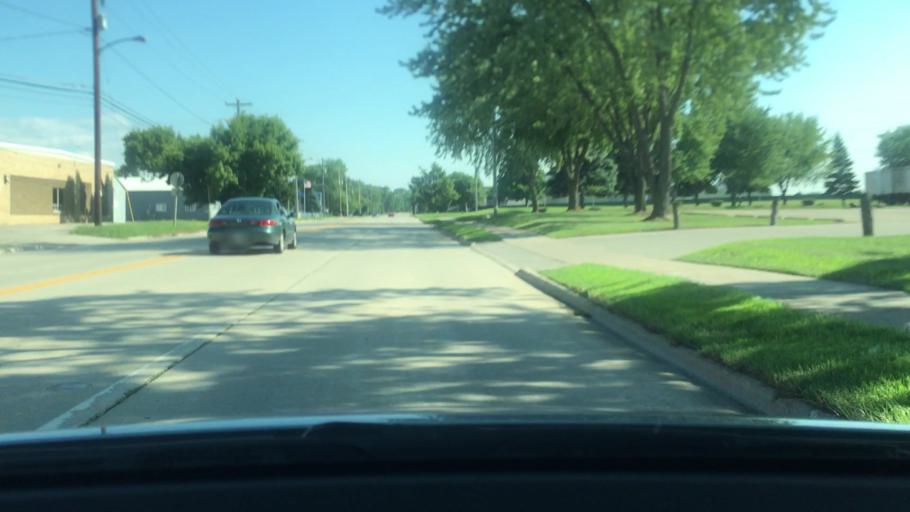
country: US
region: Wisconsin
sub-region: Winnebago County
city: Oshkosh
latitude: 43.9851
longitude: -88.5426
